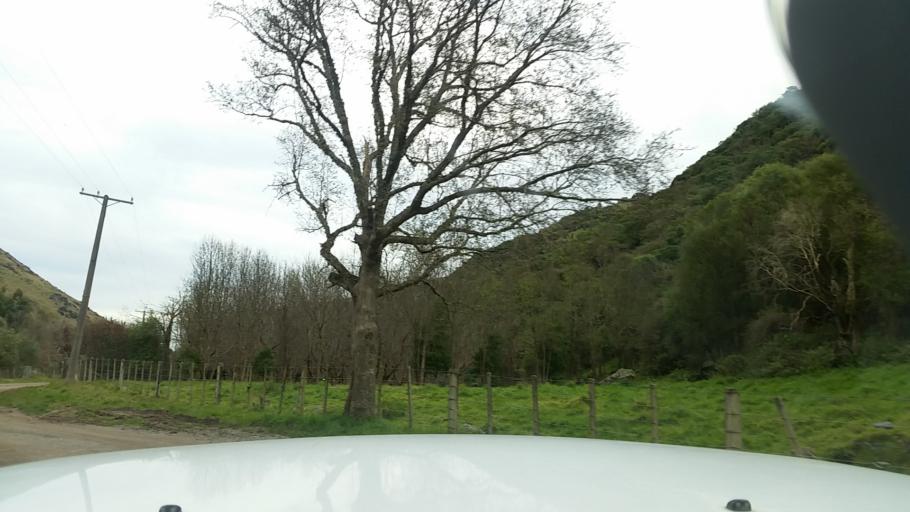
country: NZ
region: Canterbury
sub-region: Christchurch City
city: Christchurch
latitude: -43.7604
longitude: 172.7261
